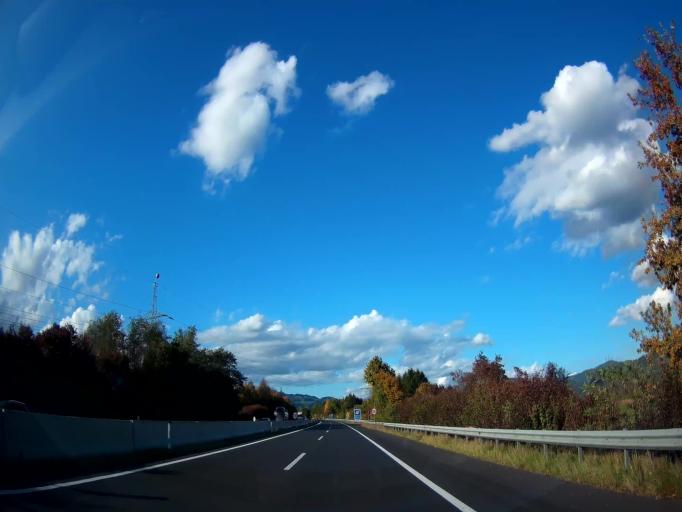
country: AT
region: Carinthia
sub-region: Politischer Bezirk Wolfsberg
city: Wolfsberg
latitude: 46.8153
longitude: 14.8229
